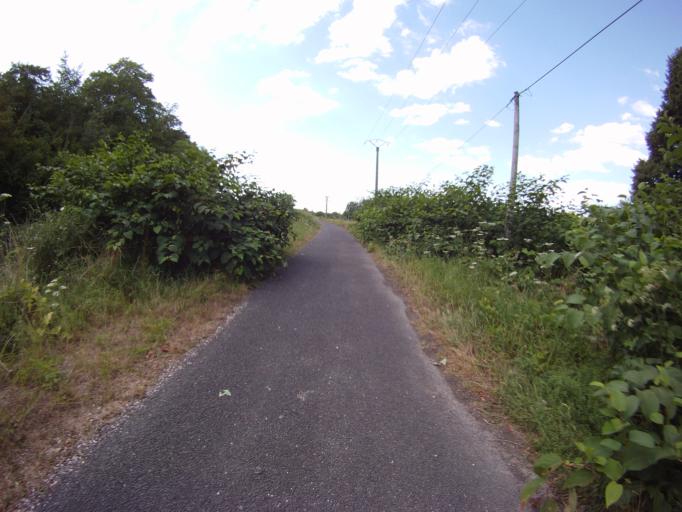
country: FR
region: Lorraine
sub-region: Departement de la Meuse
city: Longeville-en-Barrois
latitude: 48.7395
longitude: 5.2068
